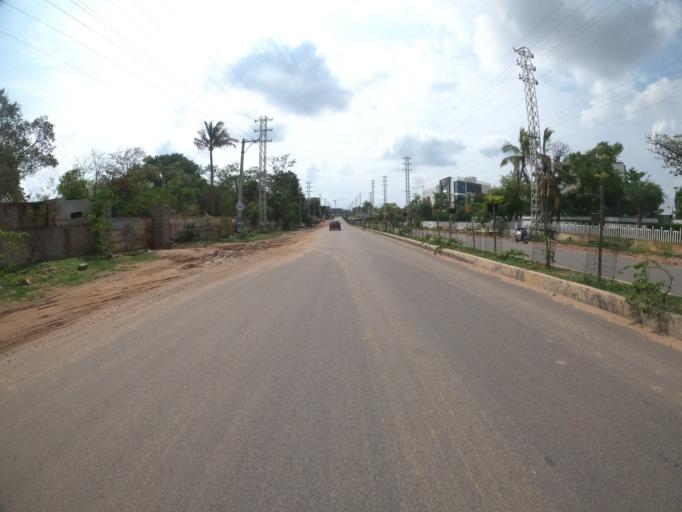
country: IN
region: Telangana
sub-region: Medak
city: Serilingampalle
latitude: 17.3866
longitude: 78.3295
